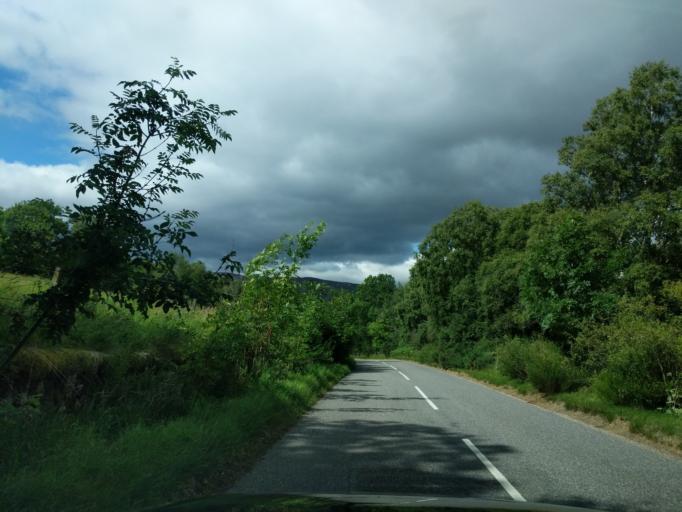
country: GB
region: Scotland
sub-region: Aberdeenshire
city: Ballater
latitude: 57.0563
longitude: -2.9370
